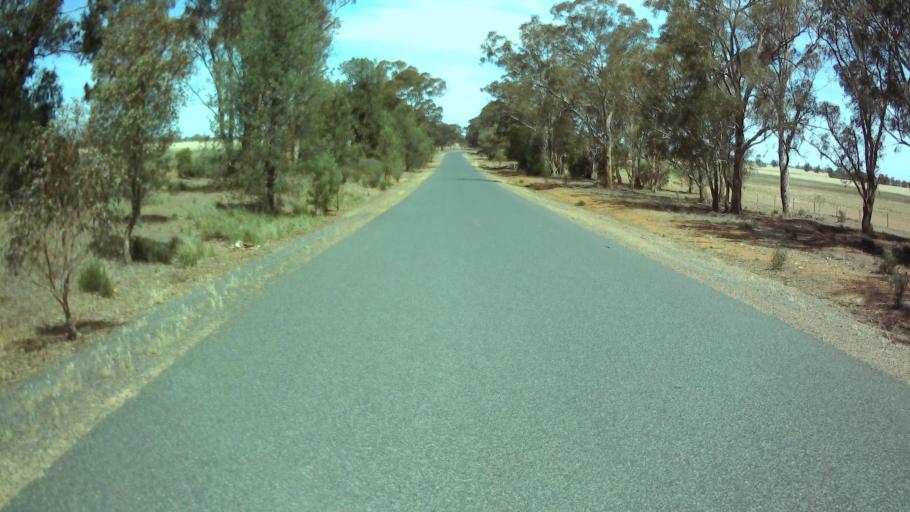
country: AU
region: New South Wales
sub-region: Weddin
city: Grenfell
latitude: -33.9058
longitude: 147.7615
